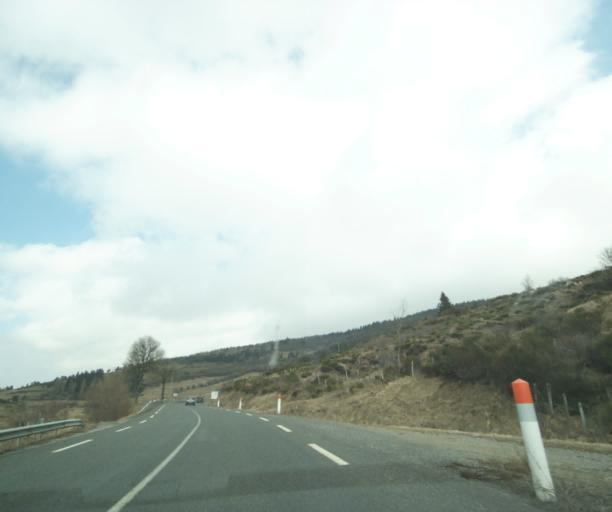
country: FR
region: Languedoc-Roussillon
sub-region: Departement de la Lozere
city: Mende
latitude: 44.6145
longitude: 3.6772
